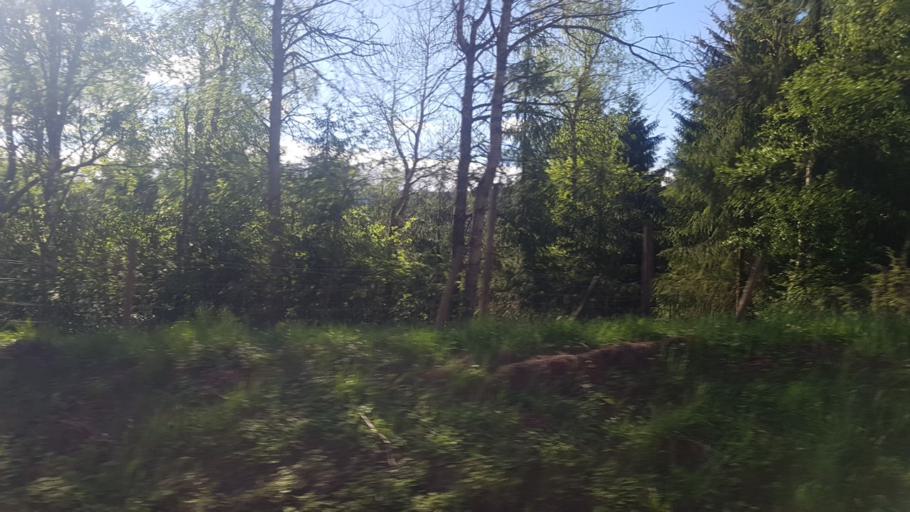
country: NO
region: Sor-Trondelag
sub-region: Midtre Gauldal
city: Storen
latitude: 62.9680
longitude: 10.2001
